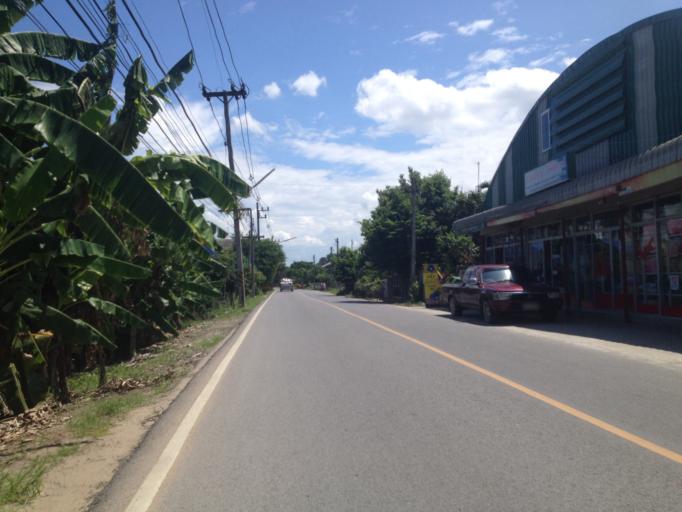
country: TH
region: Chiang Mai
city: San Pa Tong
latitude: 18.6294
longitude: 98.9340
